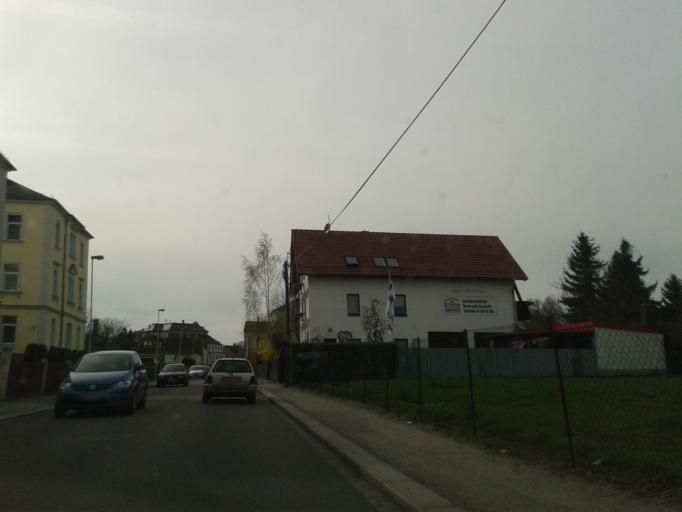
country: DE
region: Saxony
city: Radebeul
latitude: 51.0955
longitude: 13.6629
